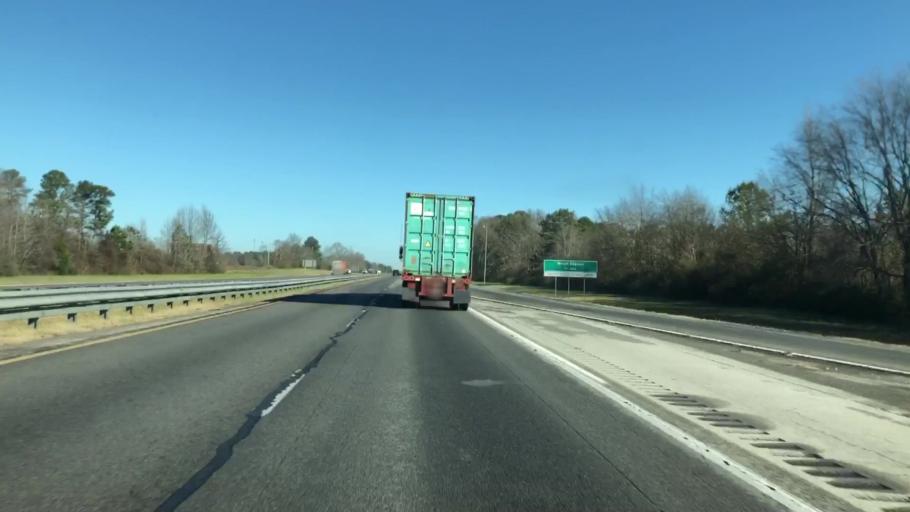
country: US
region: Alabama
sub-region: Limestone County
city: Athens
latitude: 34.8345
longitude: -86.9374
